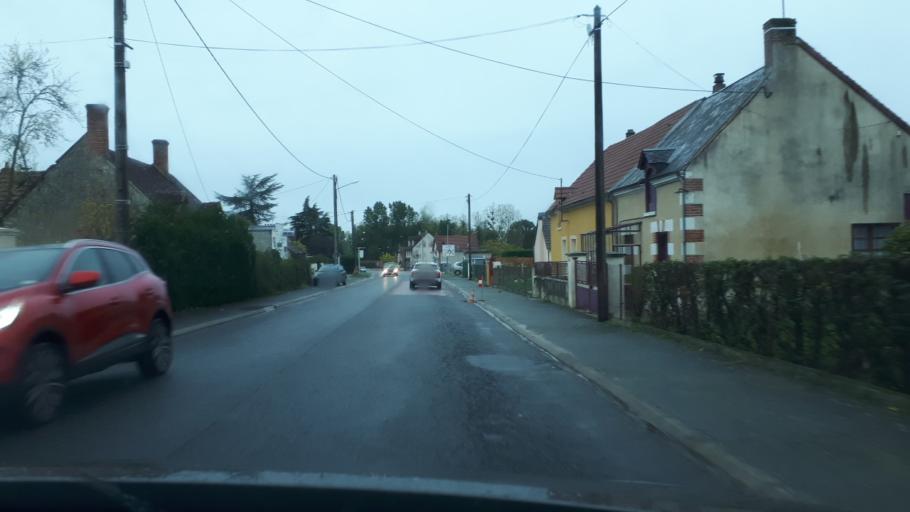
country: FR
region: Centre
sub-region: Departement du Loir-et-Cher
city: Gievres
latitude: 47.2775
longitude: 1.6657
